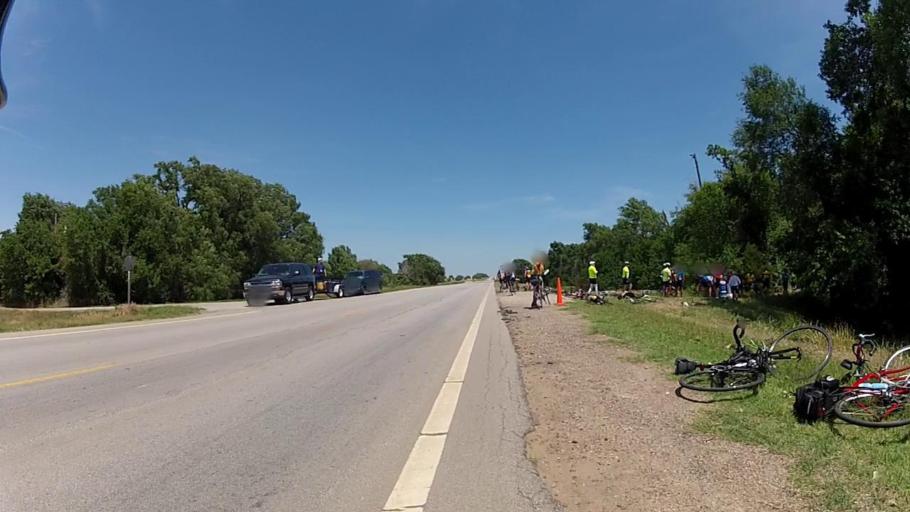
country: US
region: Kansas
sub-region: Harper County
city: Harper
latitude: 37.2388
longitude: -98.0942
